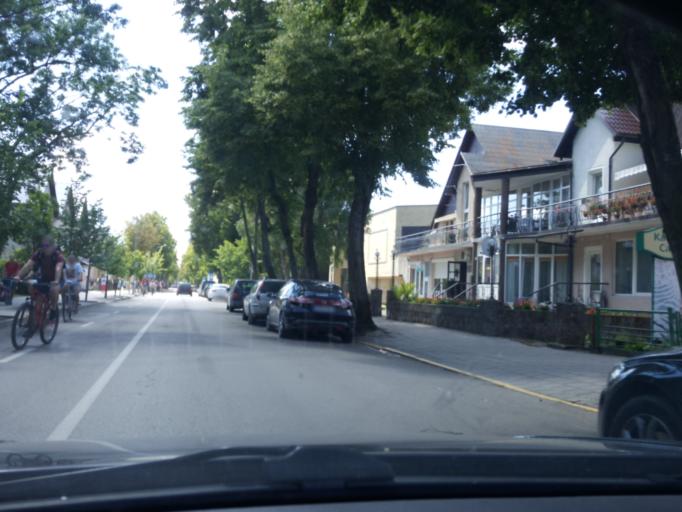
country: LT
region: Klaipedos apskritis
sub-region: Klaipeda
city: Palanga
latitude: 55.9242
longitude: 21.0703
